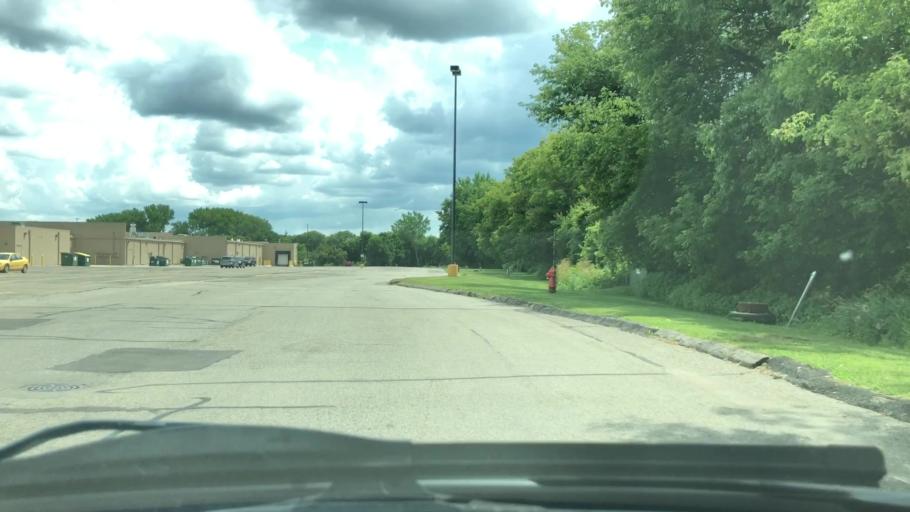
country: US
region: Minnesota
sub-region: Olmsted County
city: Rochester
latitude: 44.0774
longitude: -92.5170
